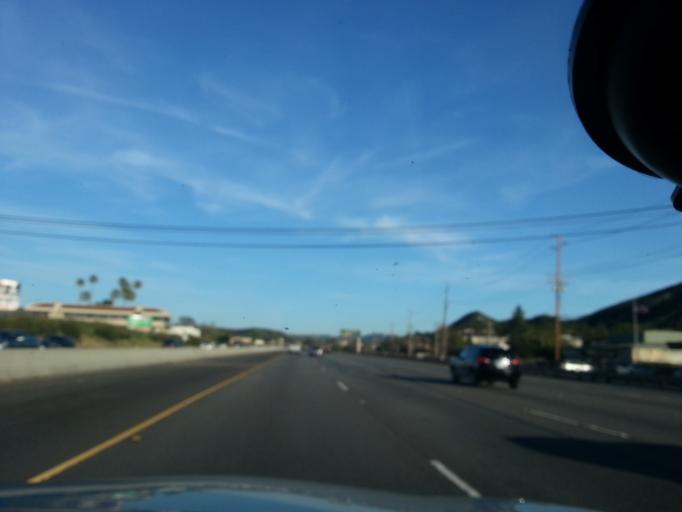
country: US
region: California
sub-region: Los Angeles County
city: Agoura
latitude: 34.1451
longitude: -118.7545
